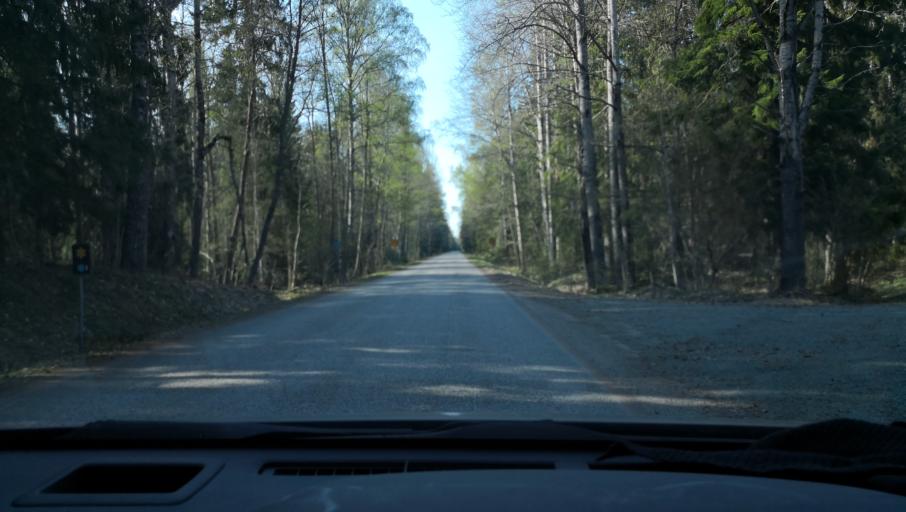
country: SE
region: Uppsala
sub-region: Heby Kommun
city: Tarnsjo
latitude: 60.2706
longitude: 16.9075
